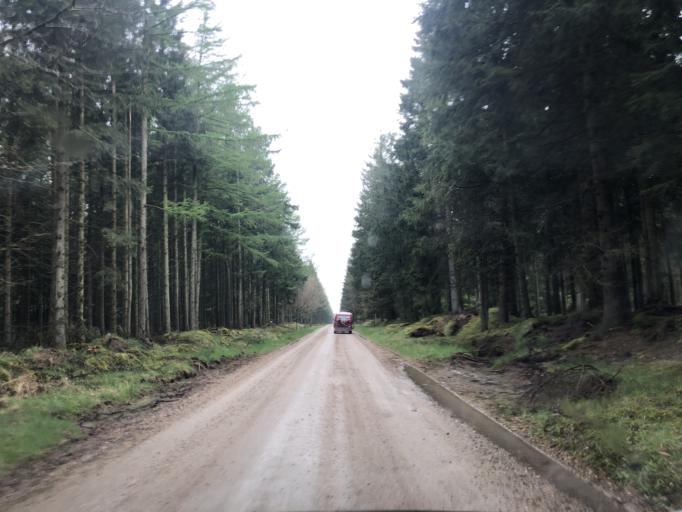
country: DK
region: Central Jutland
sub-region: Lemvig Kommune
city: Lemvig
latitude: 56.4673
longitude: 8.3911
